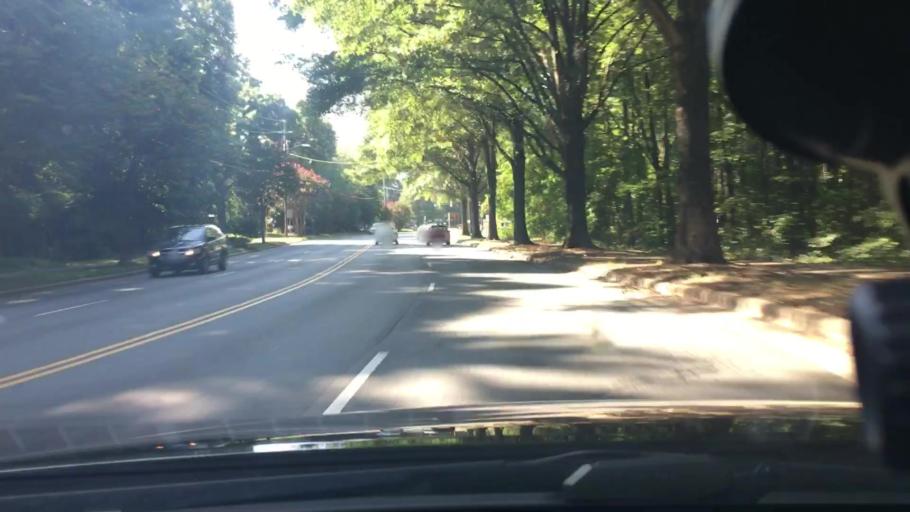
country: US
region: North Carolina
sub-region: Mecklenburg County
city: Matthews
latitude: 35.1959
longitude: -80.7264
